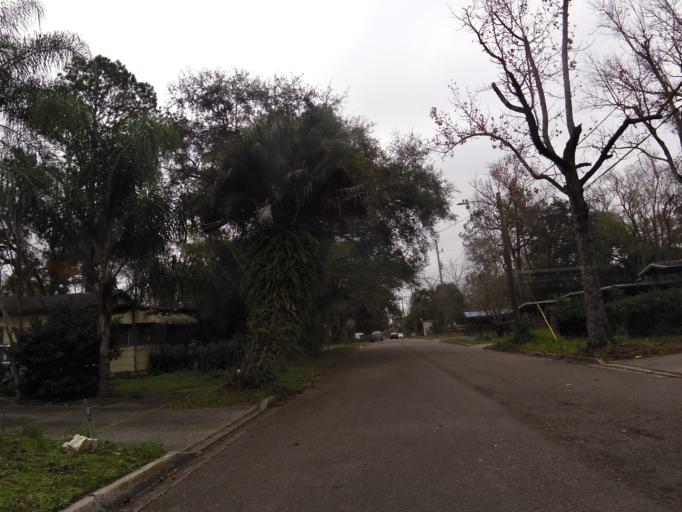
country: US
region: Florida
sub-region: Duval County
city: Jacksonville
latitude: 30.3593
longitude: -81.6906
